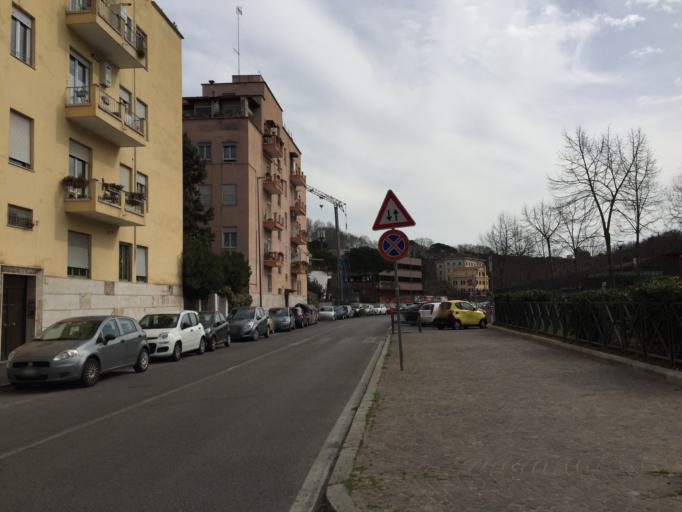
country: VA
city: Vatican City
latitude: 41.8960
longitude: 12.4555
